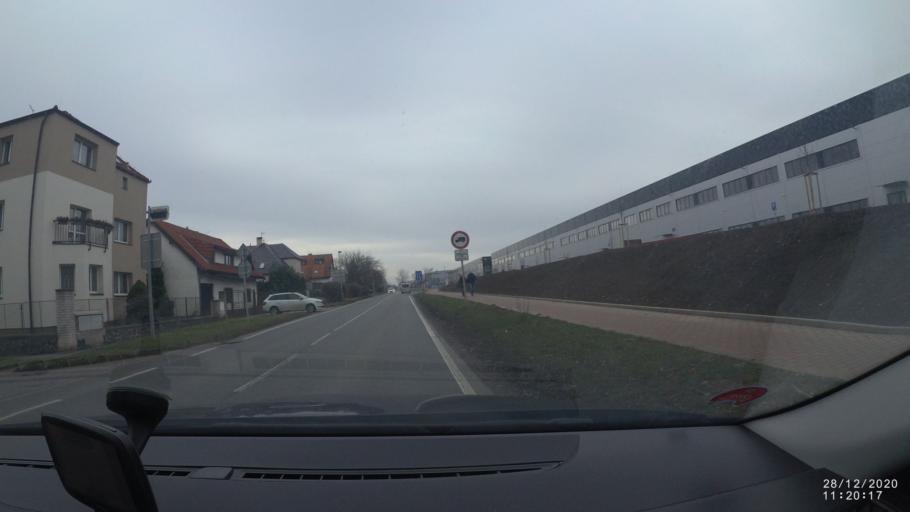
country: CZ
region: Praha
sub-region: Praha 18
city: Letnany
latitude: 50.1373
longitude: 14.5184
